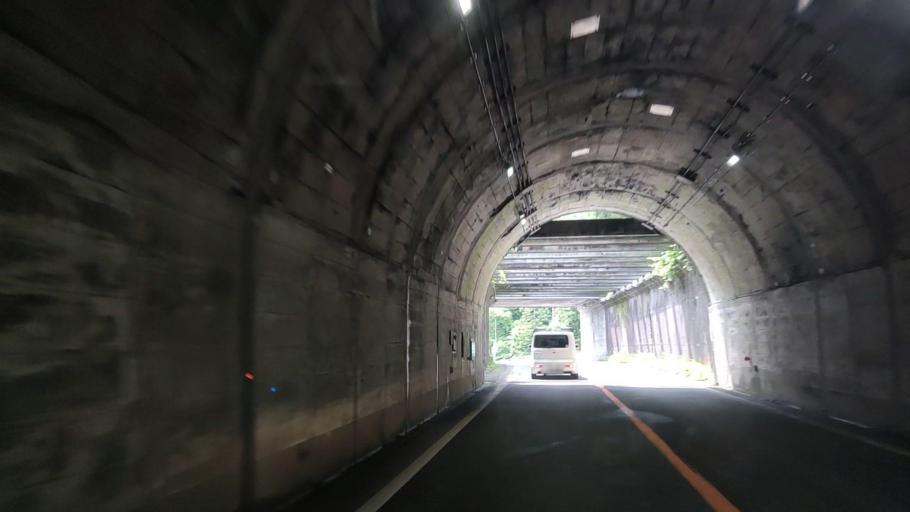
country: JP
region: Okayama
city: Niimi
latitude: 35.1842
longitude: 133.5340
